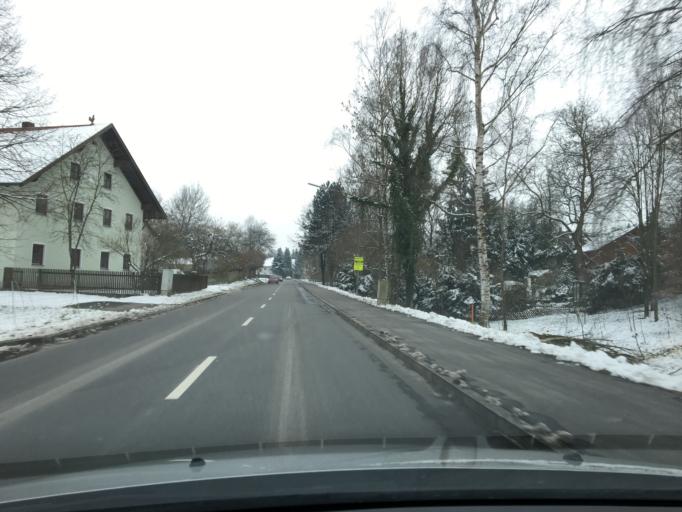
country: DE
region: Bavaria
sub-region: Lower Bavaria
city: Tiefenbach
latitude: 48.5072
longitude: 12.0986
